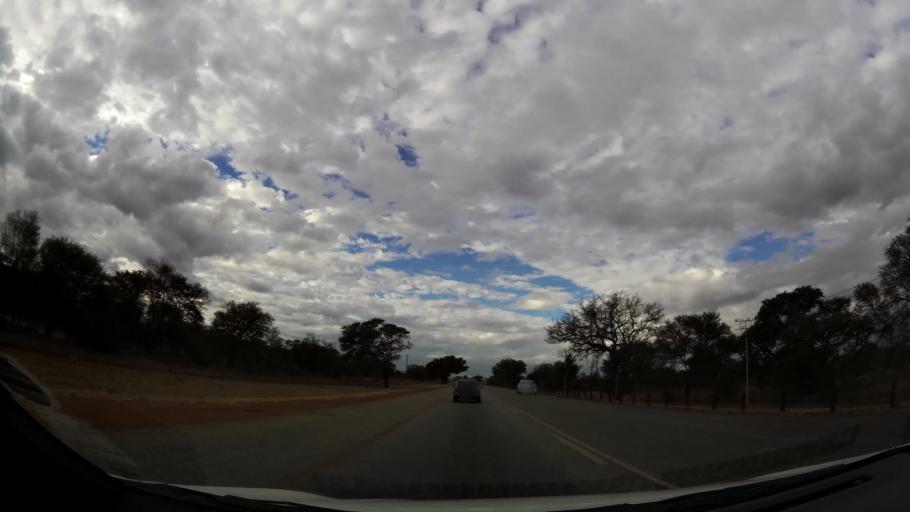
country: ZA
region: Limpopo
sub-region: Waterberg District Municipality
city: Modimolle
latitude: -24.5327
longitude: 28.7014
